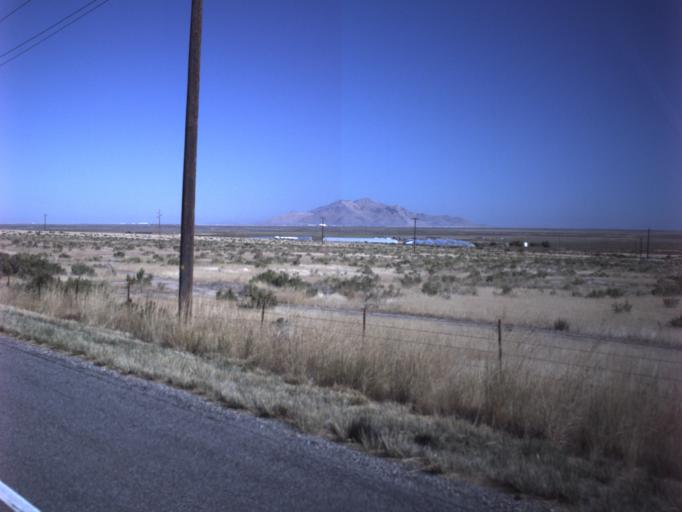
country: US
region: Utah
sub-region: Tooele County
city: Grantsville
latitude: 40.6240
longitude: -112.5065
